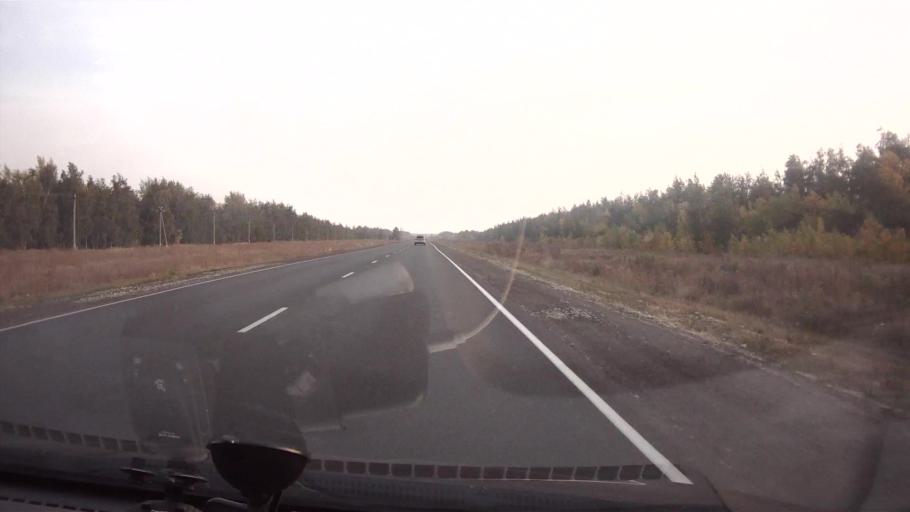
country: RU
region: Saratov
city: Krasnyy Oktyabr'
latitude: 51.3727
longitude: 45.7124
